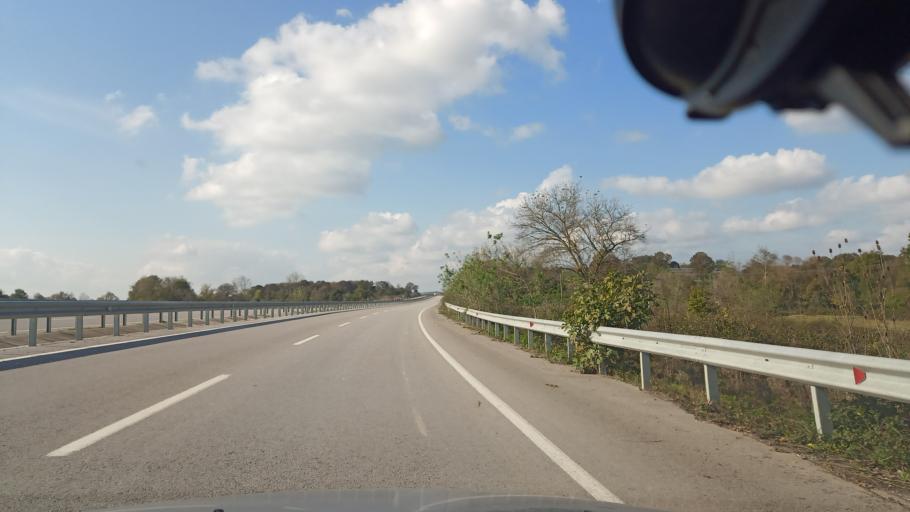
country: TR
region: Sakarya
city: Kaynarca
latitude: 41.0726
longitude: 30.3958
